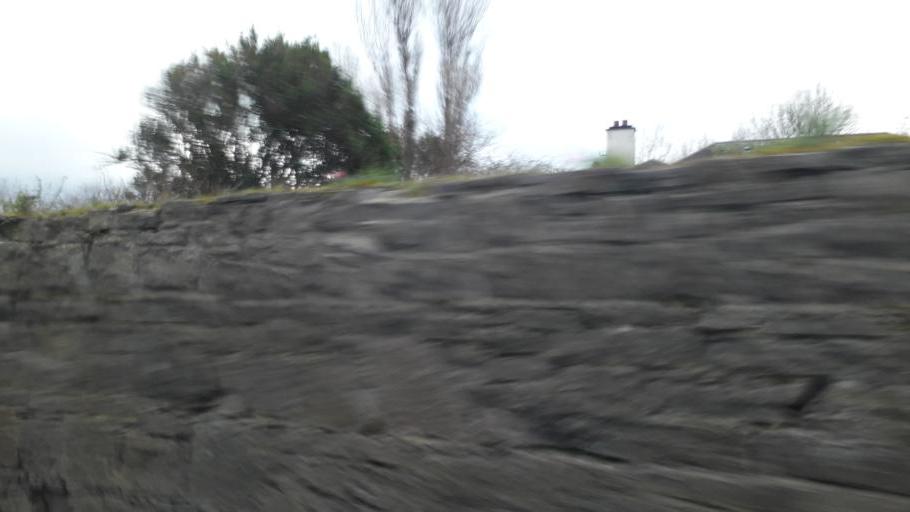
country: IE
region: Leinster
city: An Ros
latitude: 53.5330
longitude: -6.0910
